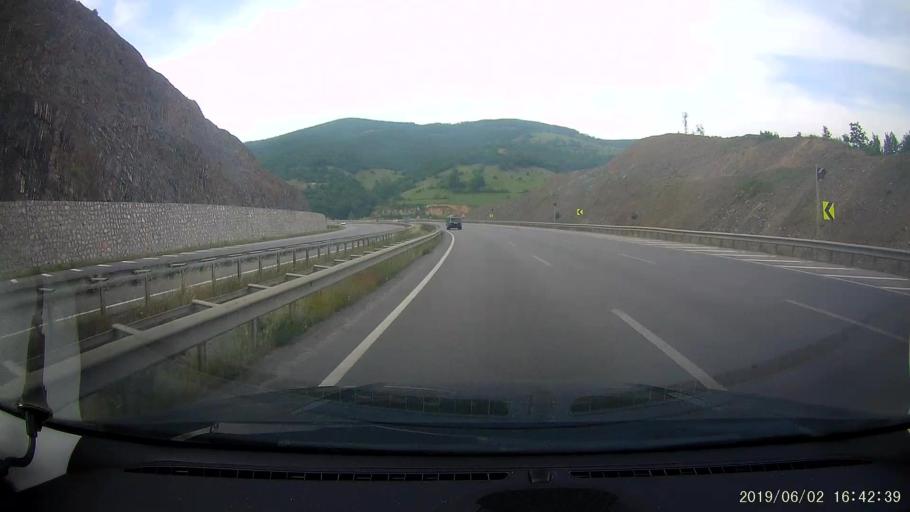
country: TR
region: Samsun
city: Kavak
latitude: 41.1211
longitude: 36.1371
